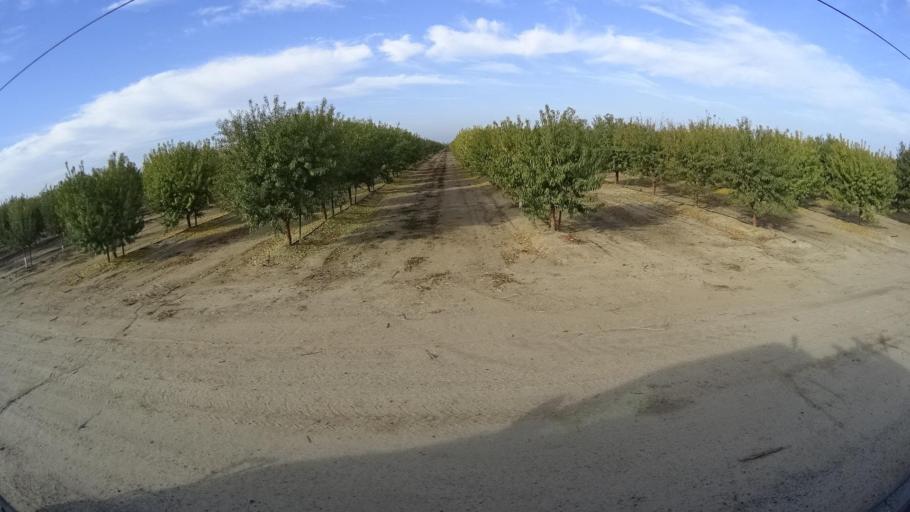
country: US
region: California
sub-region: Kern County
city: Delano
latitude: 35.7593
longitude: -119.2053
